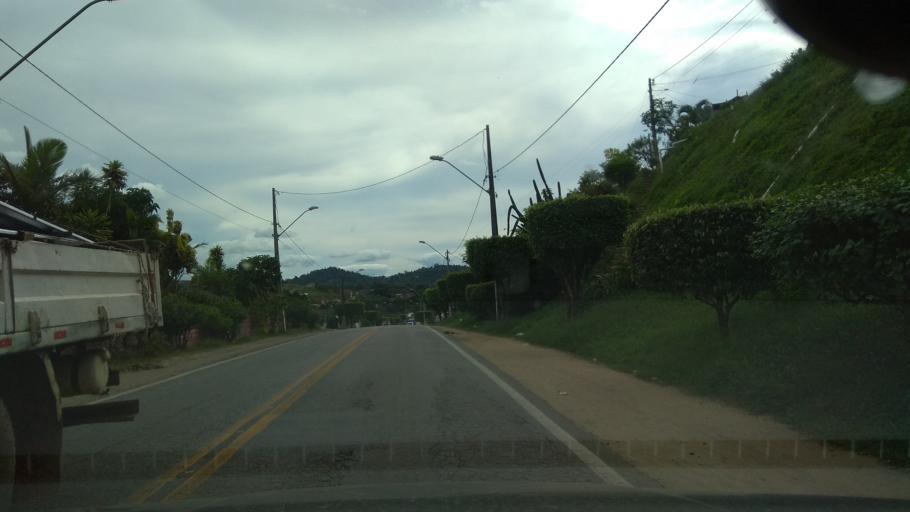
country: BR
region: Bahia
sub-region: Ubata
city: Ubata
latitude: -14.2113
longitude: -39.5207
